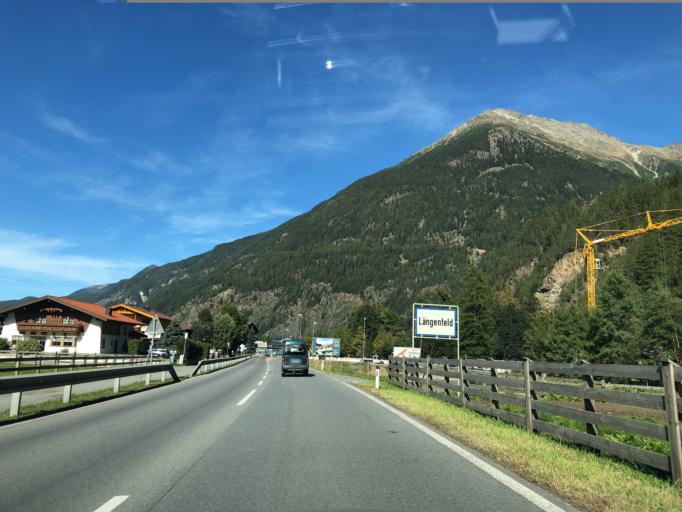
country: AT
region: Tyrol
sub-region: Politischer Bezirk Imst
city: Umhausen
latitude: 47.0638
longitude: 10.9671
